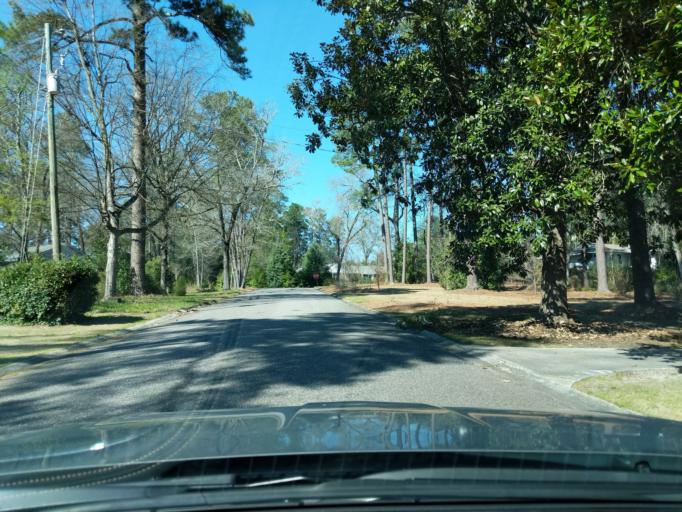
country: US
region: South Carolina
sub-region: Aiken County
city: Aiken
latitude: 33.5311
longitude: -81.7372
